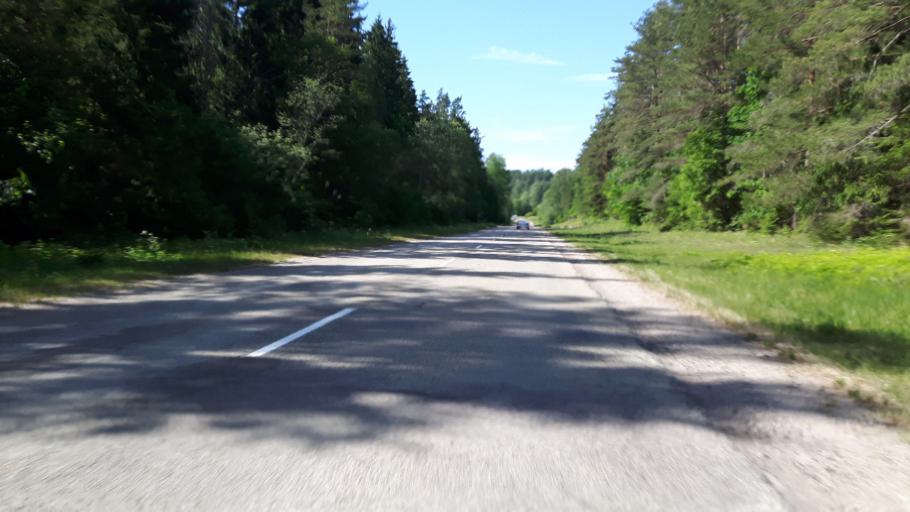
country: LV
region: Talsu Rajons
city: Sabile
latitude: 57.0809
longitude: 22.5277
